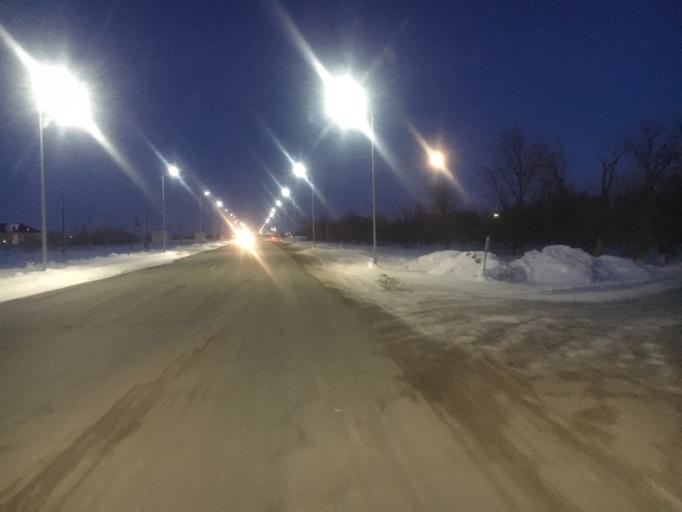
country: KZ
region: Batys Qazaqstan
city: Oral
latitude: 51.1570
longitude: 51.4976
